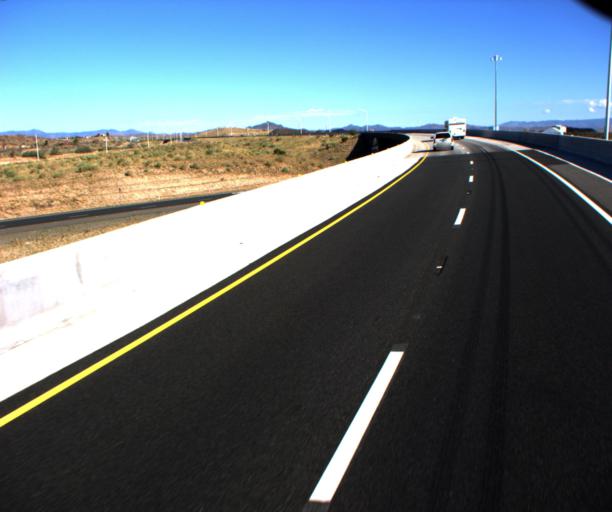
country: US
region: Arizona
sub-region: Yavapai County
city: Cordes Lakes
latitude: 34.3275
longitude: -112.1207
